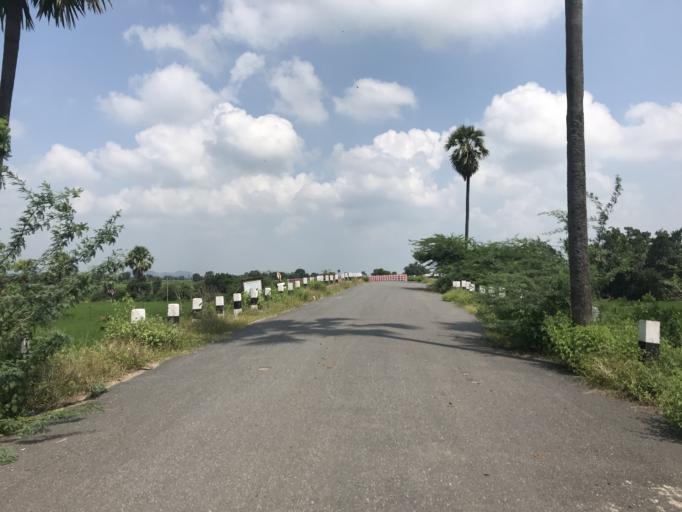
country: IN
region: Telangana
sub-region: Warangal
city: Mahbubabad
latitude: 17.6852
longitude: 79.7123
